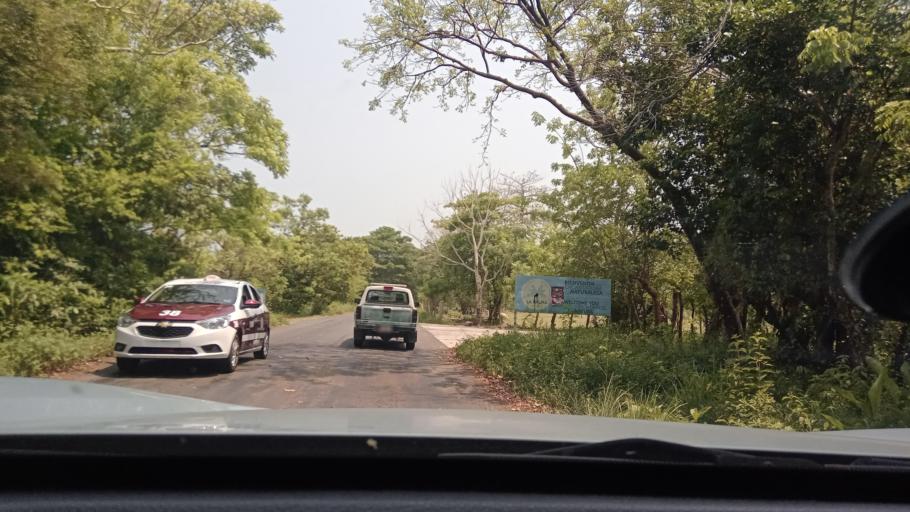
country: MX
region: Veracruz
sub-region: San Andres Tuxtla
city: Santa Rosa Abata
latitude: 18.5600
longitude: -95.0591
